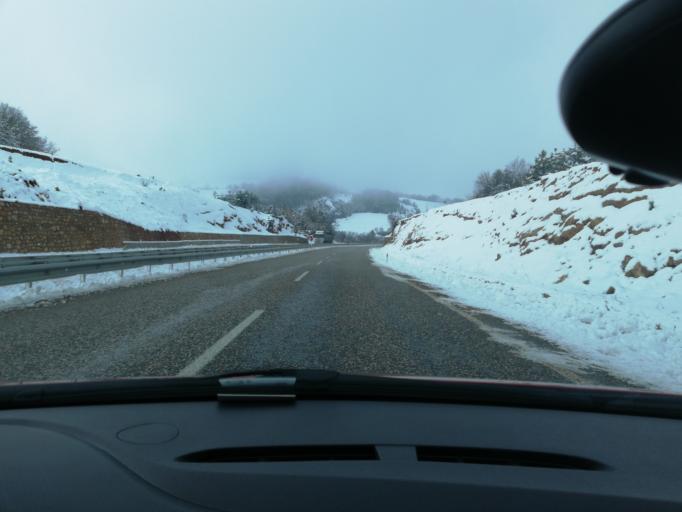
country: TR
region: Kastamonu
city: Akkaya
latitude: 41.2822
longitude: 33.4667
